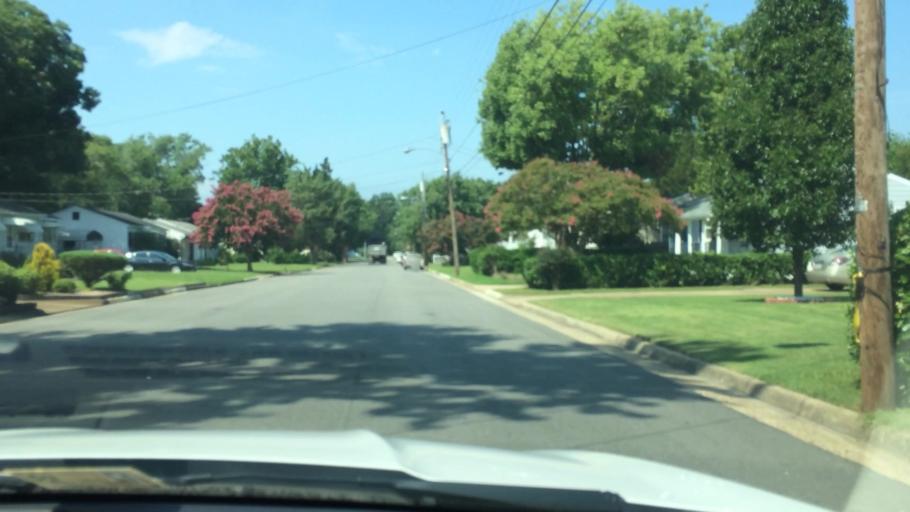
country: US
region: Virginia
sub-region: City of Newport News
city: Newport News
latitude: 37.0201
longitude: -76.4278
